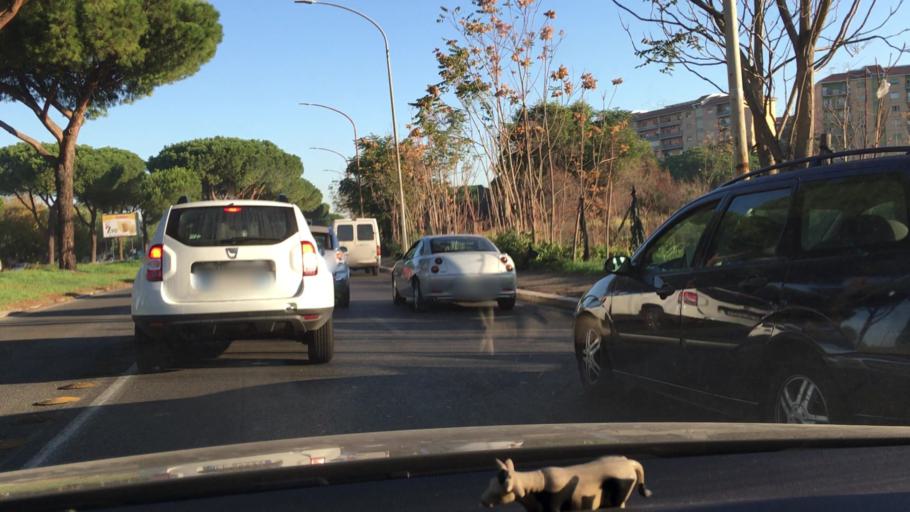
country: IT
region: Latium
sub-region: Citta metropolitana di Roma Capitale
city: Rome
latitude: 41.8669
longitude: 12.5679
